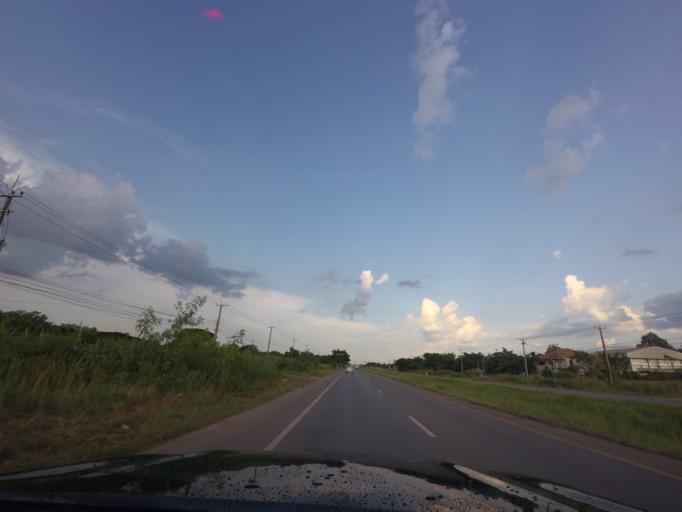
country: TH
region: Khon Kaen
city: Khon Kaen
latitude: 16.3972
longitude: 102.8607
